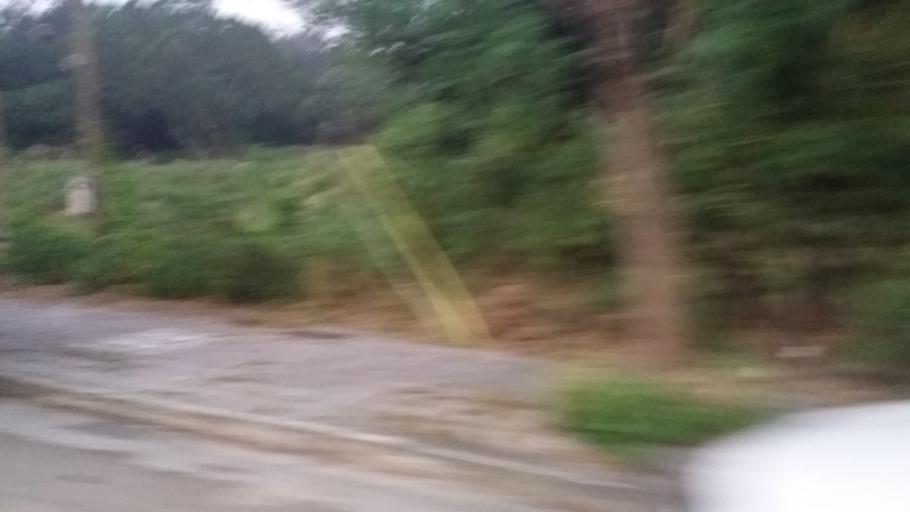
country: TW
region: Taiwan
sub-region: Hsinchu
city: Hsinchu
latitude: 24.7327
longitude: 120.9149
